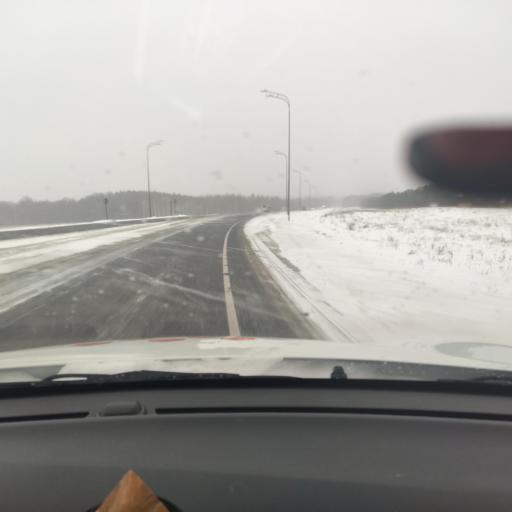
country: RU
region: Tatarstan
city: Verkhniy Uslon
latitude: 55.7049
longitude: 48.8901
